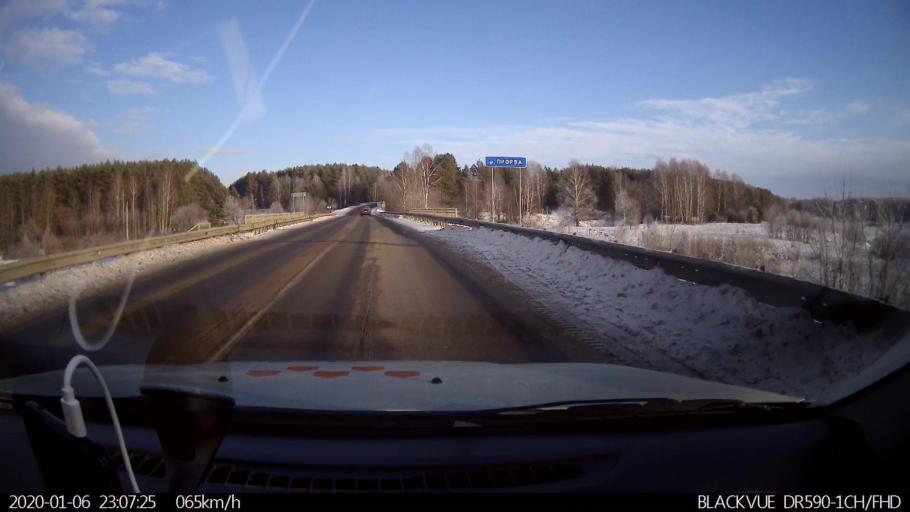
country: RU
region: Nizjnij Novgorod
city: Bogorodsk
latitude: 56.1288
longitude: 43.5902
